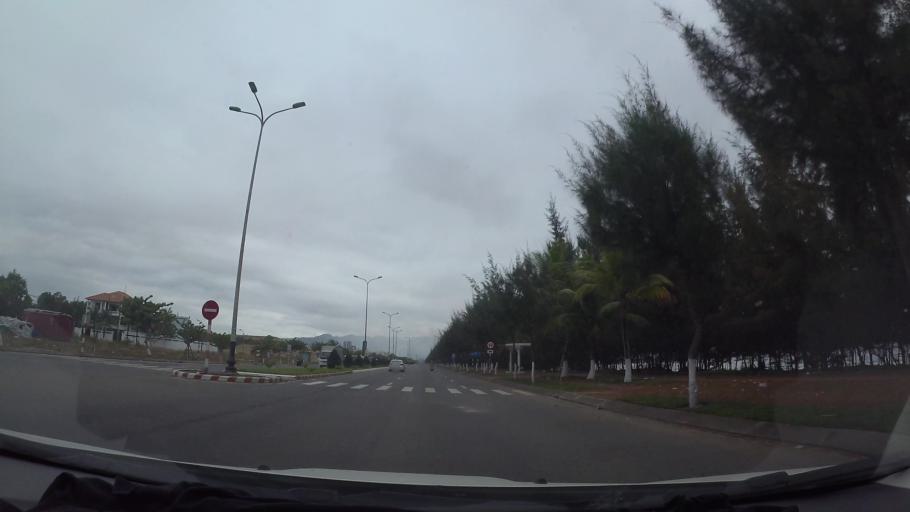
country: VN
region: Da Nang
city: Lien Chieu
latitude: 16.1011
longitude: 108.1402
